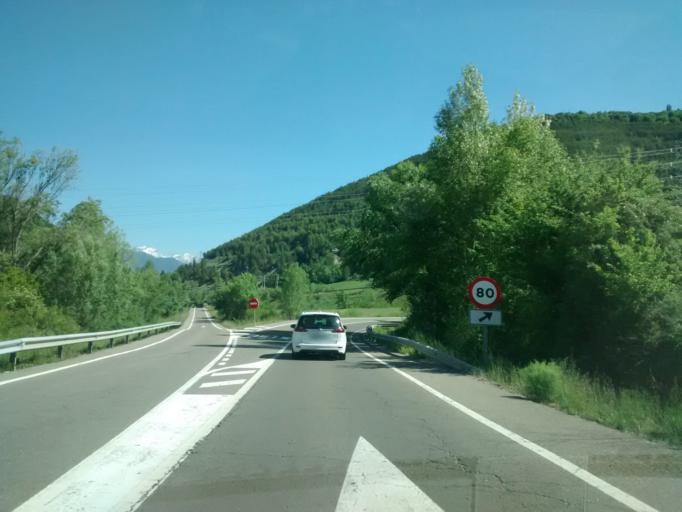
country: ES
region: Aragon
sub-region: Provincia de Huesca
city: Jaca
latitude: 42.5817
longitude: -0.5439
